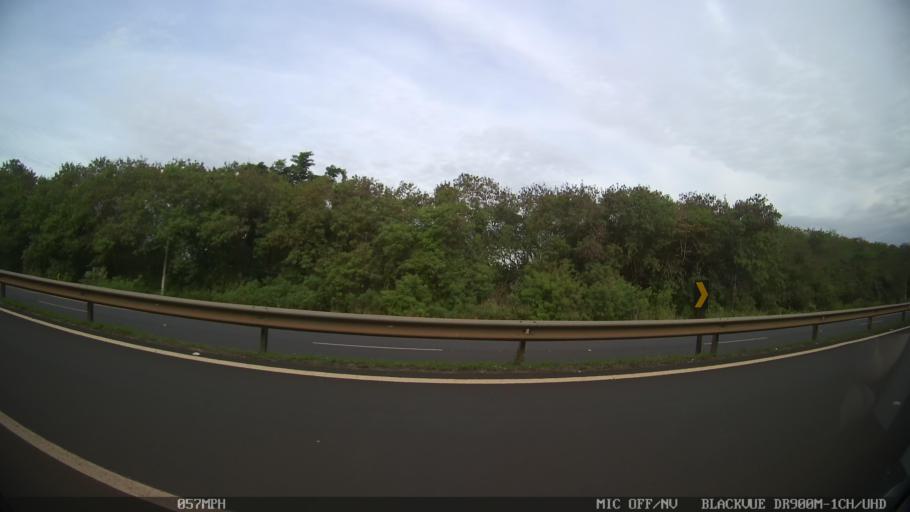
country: BR
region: Sao Paulo
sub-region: Piracicaba
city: Piracicaba
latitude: -22.6973
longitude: -47.5924
